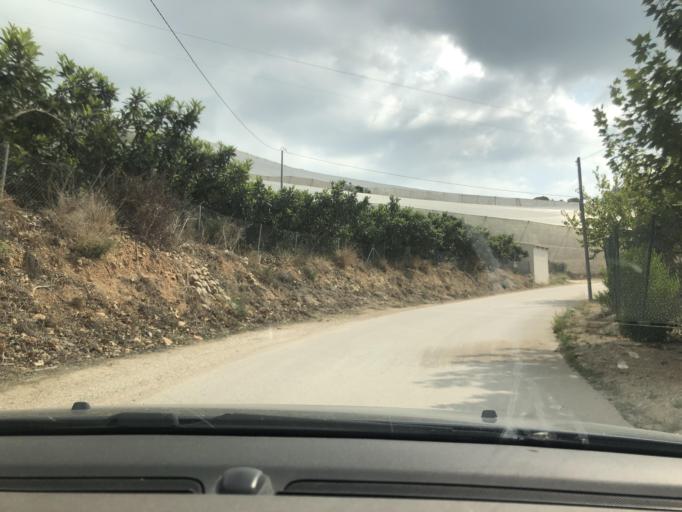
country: ES
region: Valencia
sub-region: Provincia de Alicante
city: Callosa d'En Sarria
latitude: 38.6551
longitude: -0.0931
